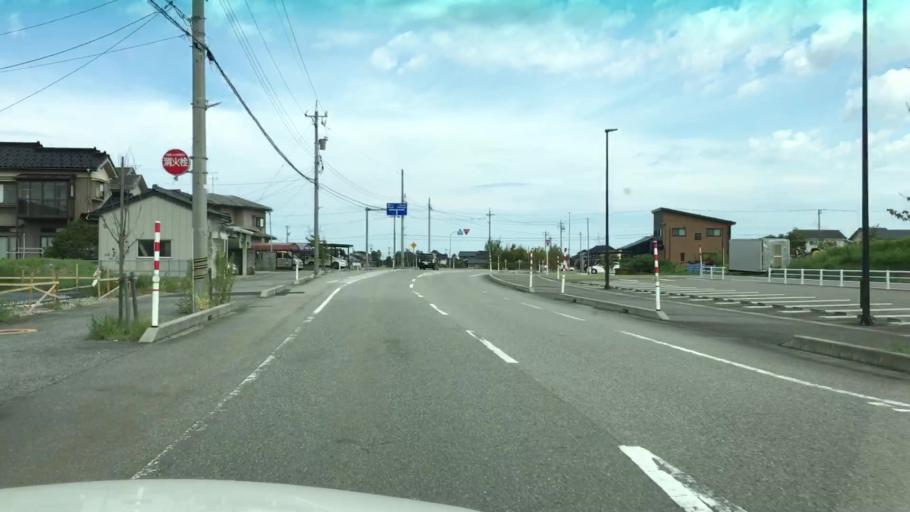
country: JP
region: Toyama
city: Kamiichi
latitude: 36.7047
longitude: 137.3419
